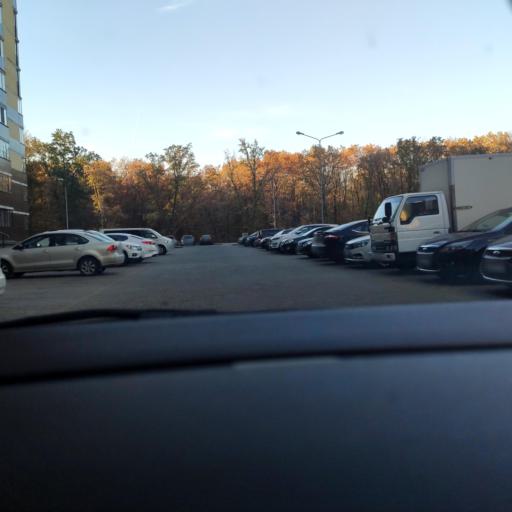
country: RU
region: Voronezj
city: Voronezh
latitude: 51.7162
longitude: 39.1970
